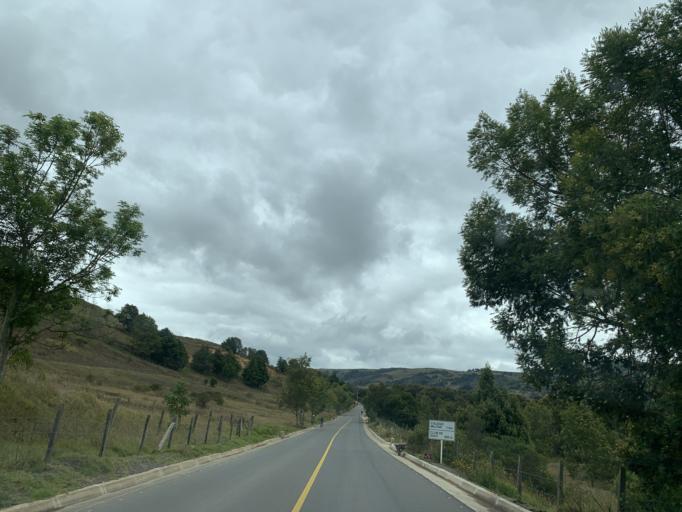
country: CO
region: Boyaca
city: Tunja
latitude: 5.5280
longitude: -73.3203
